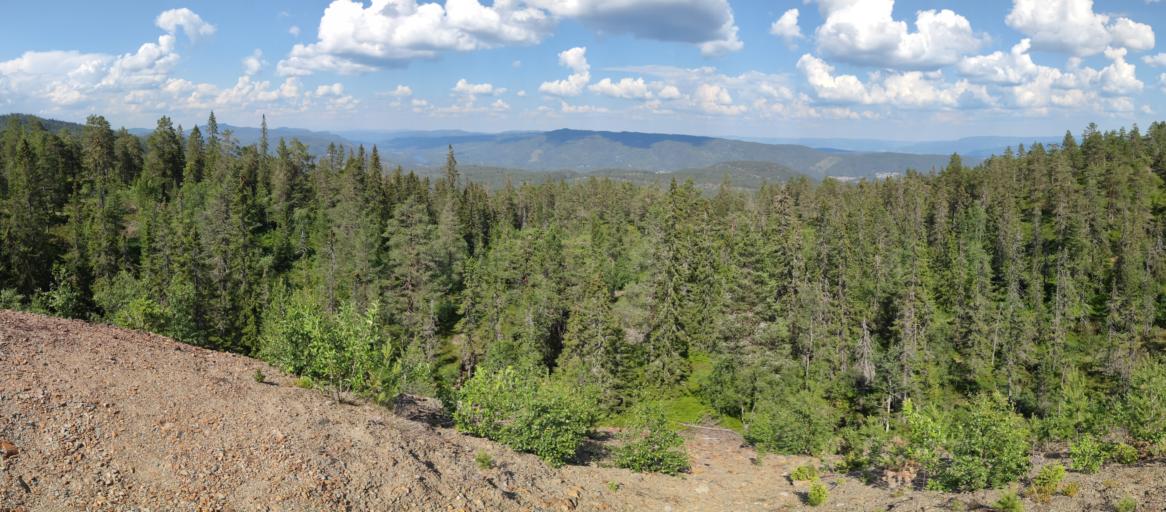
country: NO
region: Buskerud
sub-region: Kongsberg
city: Kongsberg
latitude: 59.6725
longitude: 9.5794
